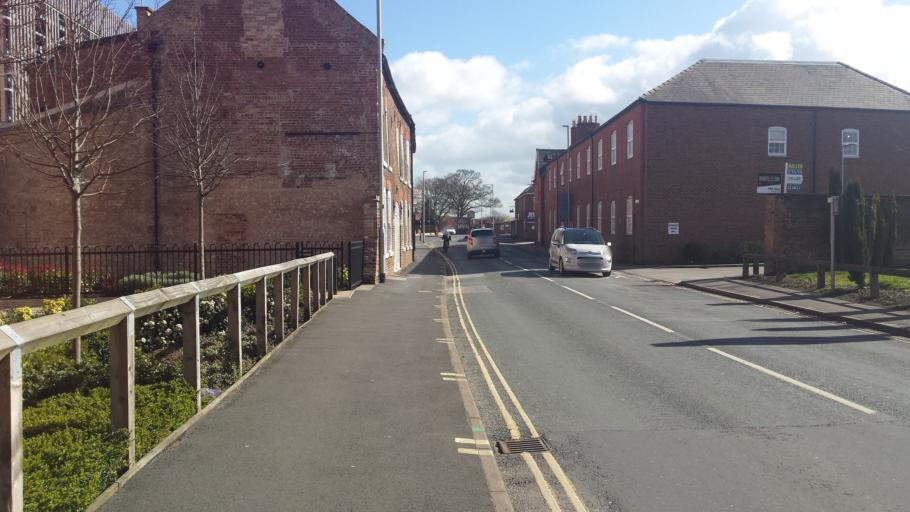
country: GB
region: England
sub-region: East Riding of Yorkshire
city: Beverley
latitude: 53.8390
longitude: -0.4217
